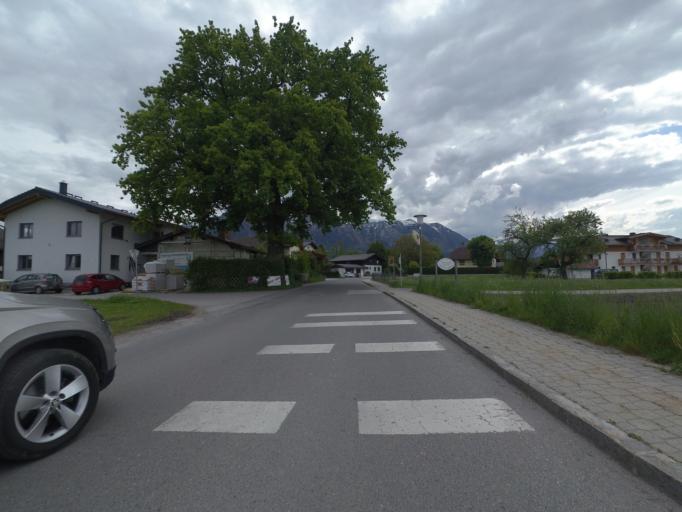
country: AT
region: Salzburg
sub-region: Politischer Bezirk Salzburg-Umgebung
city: Grodig
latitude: 47.7725
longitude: 12.9925
